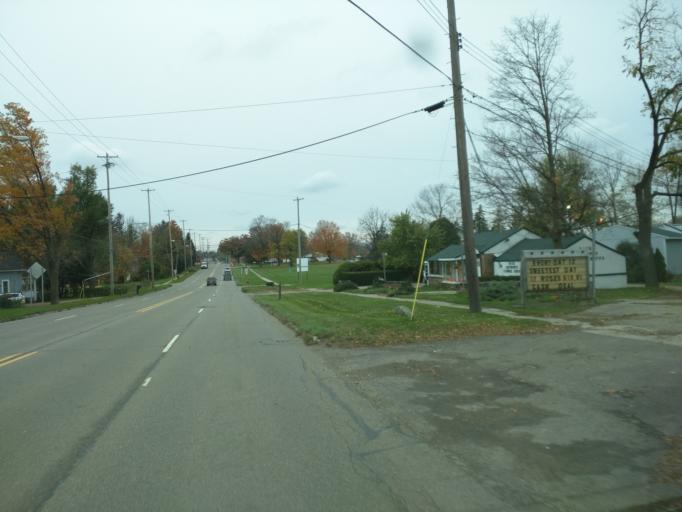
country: US
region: Michigan
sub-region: Ingham County
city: Lansing
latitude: 42.7568
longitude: -84.5616
